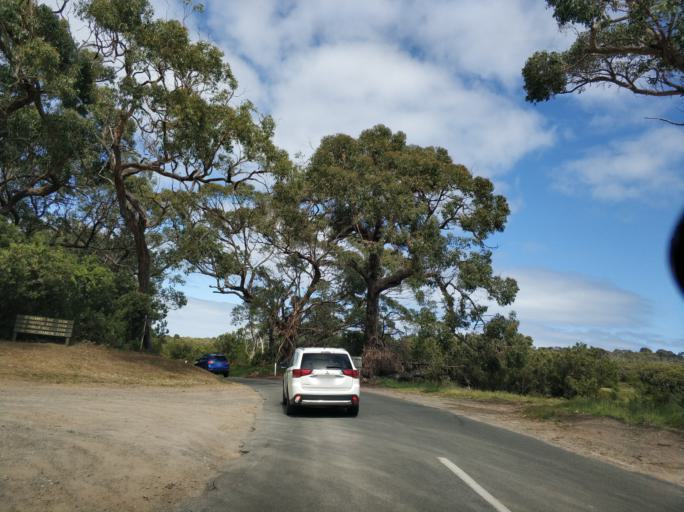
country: AU
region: Victoria
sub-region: Colac-Otway
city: Apollo Bay
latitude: -38.8434
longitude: 143.5339
